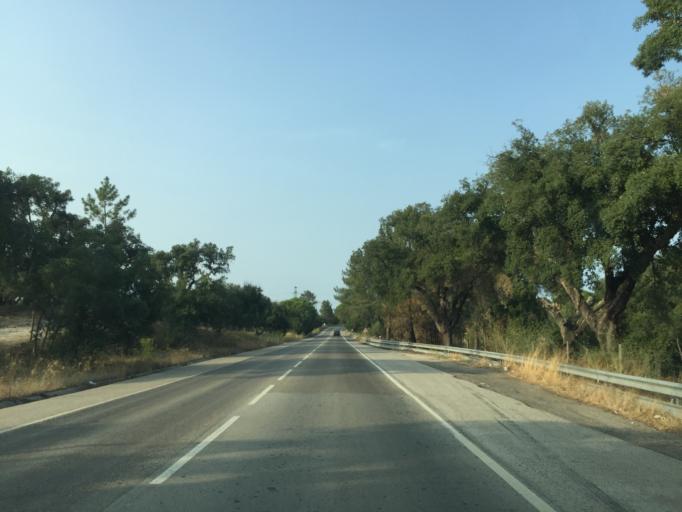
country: PT
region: Setubal
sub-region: Setubal
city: Setubal
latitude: 38.5867
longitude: -8.6783
